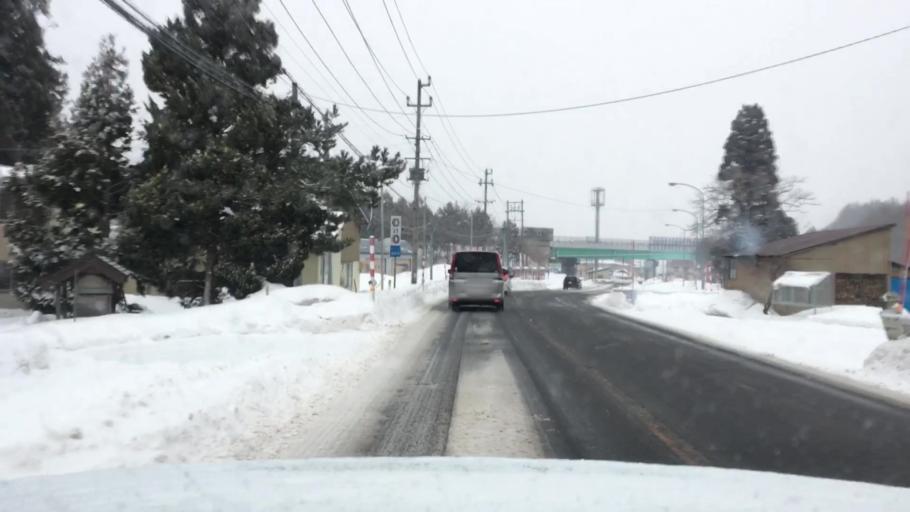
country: JP
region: Akita
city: Hanawa
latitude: 40.0449
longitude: 140.9996
